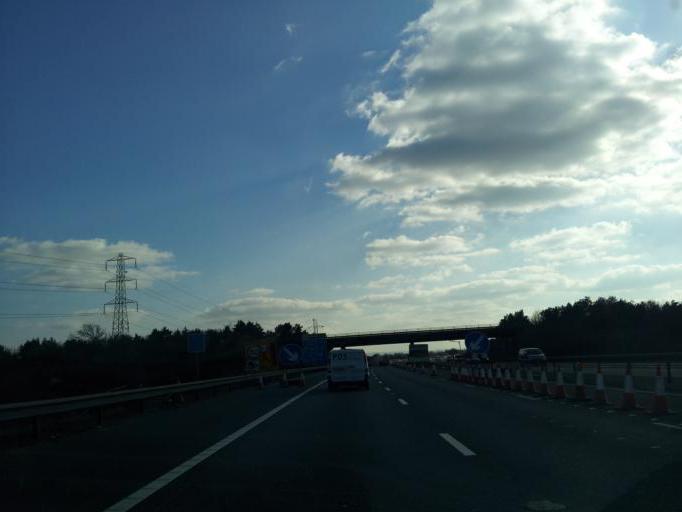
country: GB
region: England
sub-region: Somerset
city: Bridgwater
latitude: 51.1252
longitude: -2.9697
